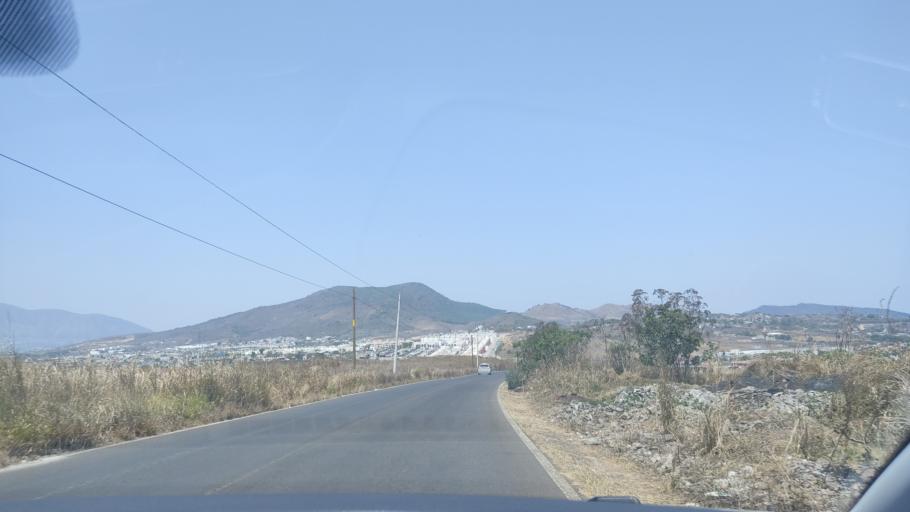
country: MX
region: Nayarit
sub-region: Tepic
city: La Corregidora
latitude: 21.4892
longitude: -104.8079
